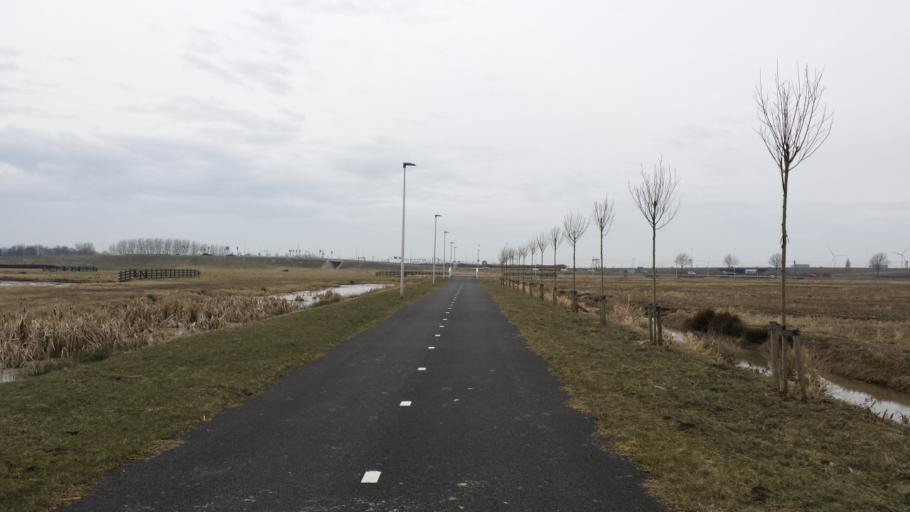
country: NL
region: South Holland
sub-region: Gemeente Gouda
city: Bloemendaal
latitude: 52.0029
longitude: 4.6654
